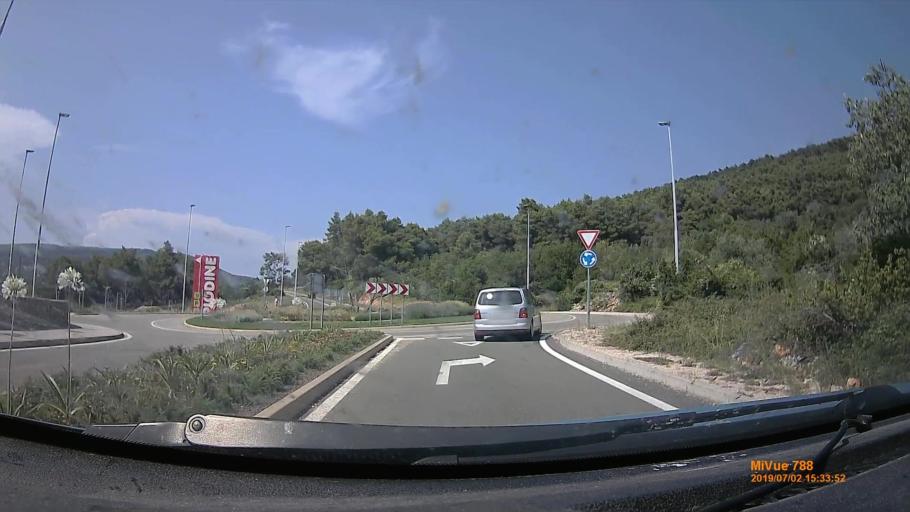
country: HR
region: Primorsko-Goranska
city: Cres
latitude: 44.9628
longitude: 14.4131
